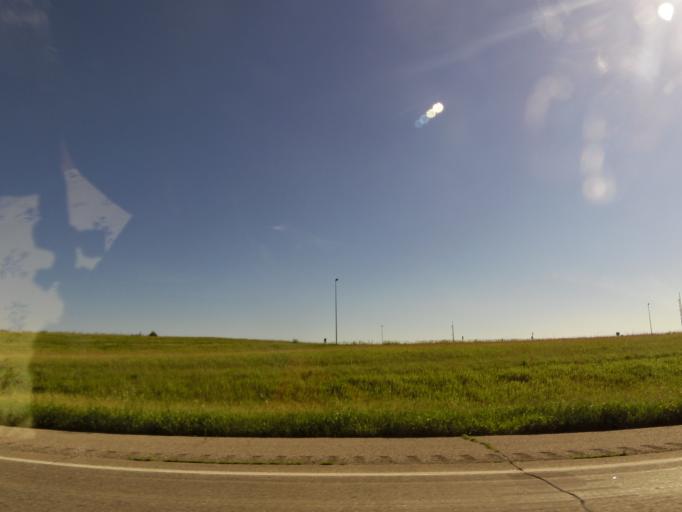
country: US
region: Minnesota
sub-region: Otter Tail County
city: Fergus Falls
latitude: 46.2504
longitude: -96.0738
